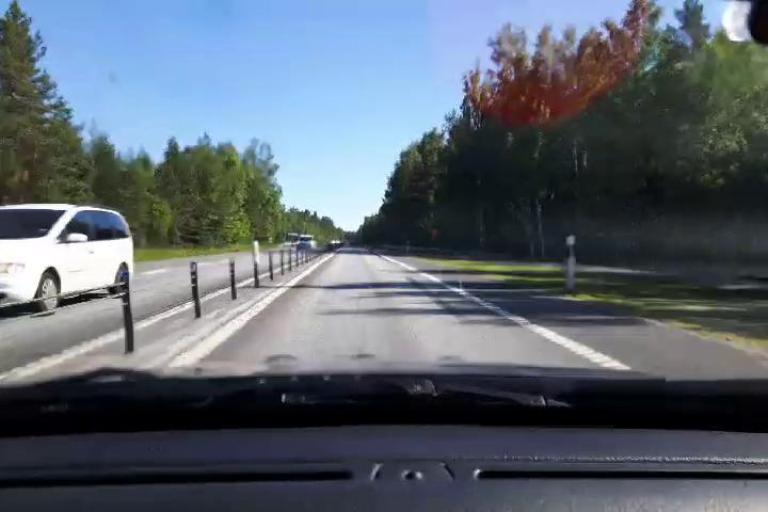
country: SE
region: Gaevleborg
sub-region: Gavle Kommun
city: Norrsundet
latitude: 61.0066
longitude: 16.9852
